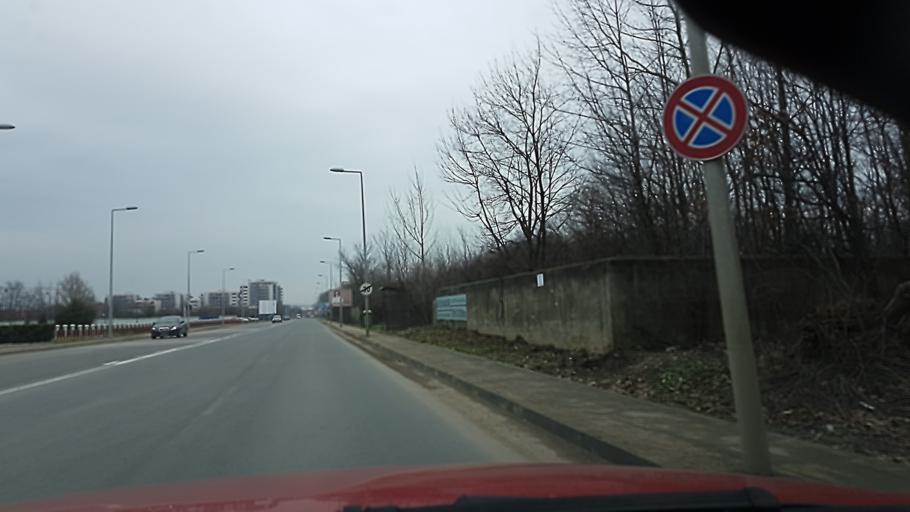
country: RO
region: Ilfov
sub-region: Comuna Tunari
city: Tunari
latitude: 44.5291
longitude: 26.1430
